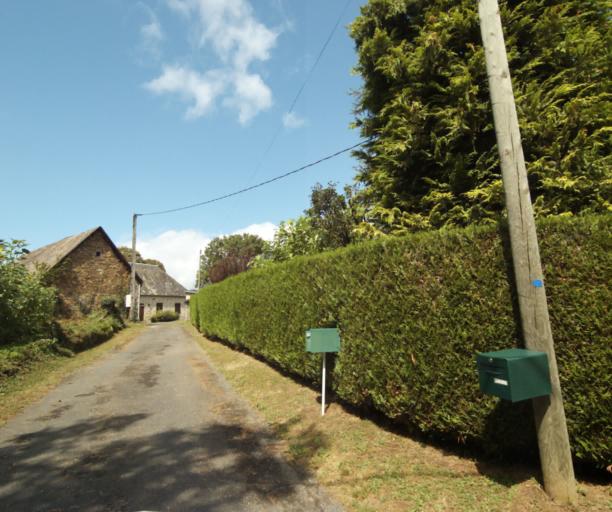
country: FR
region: Limousin
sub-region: Departement de la Correze
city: Sainte-Fortunade
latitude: 45.2006
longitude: 1.8066
